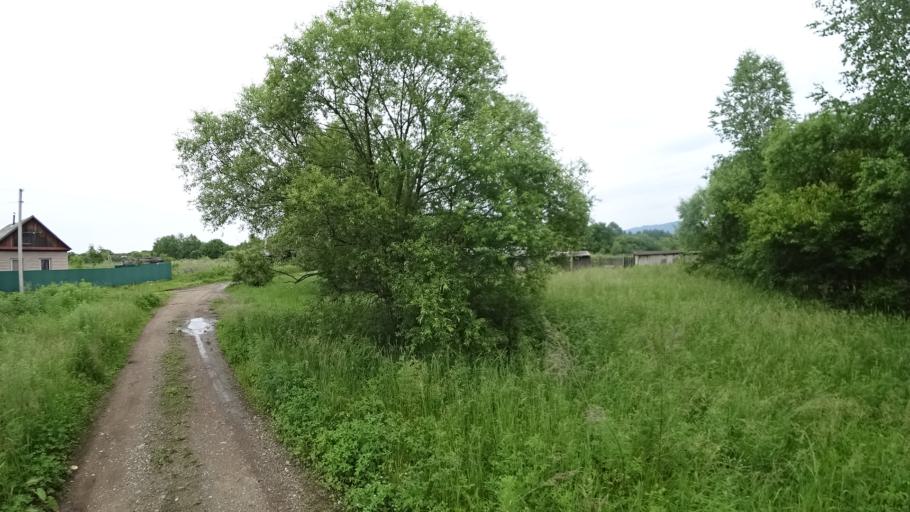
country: RU
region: Primorskiy
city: Novosysoyevka
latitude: 44.2070
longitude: 133.3264
